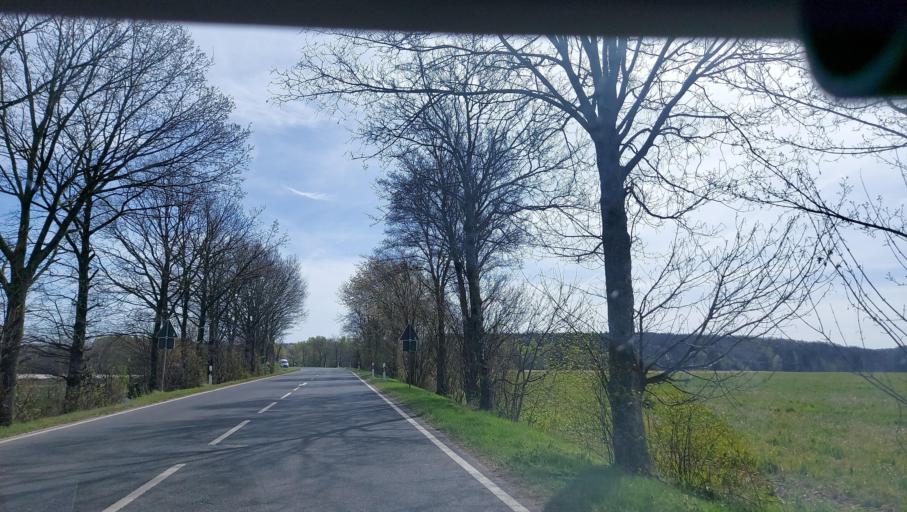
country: DE
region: North Rhine-Westphalia
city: Zulpich
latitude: 50.6545
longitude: 6.7006
